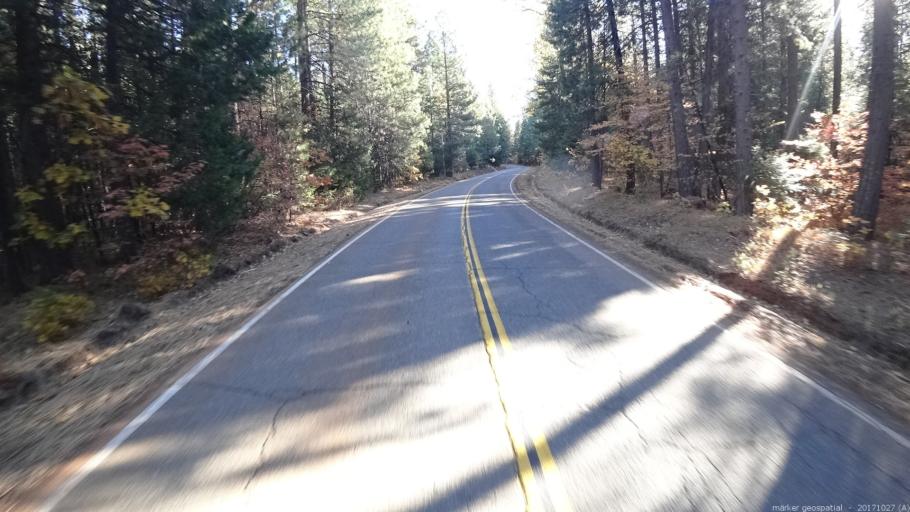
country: US
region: California
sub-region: Shasta County
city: Burney
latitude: 40.9686
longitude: -121.9328
